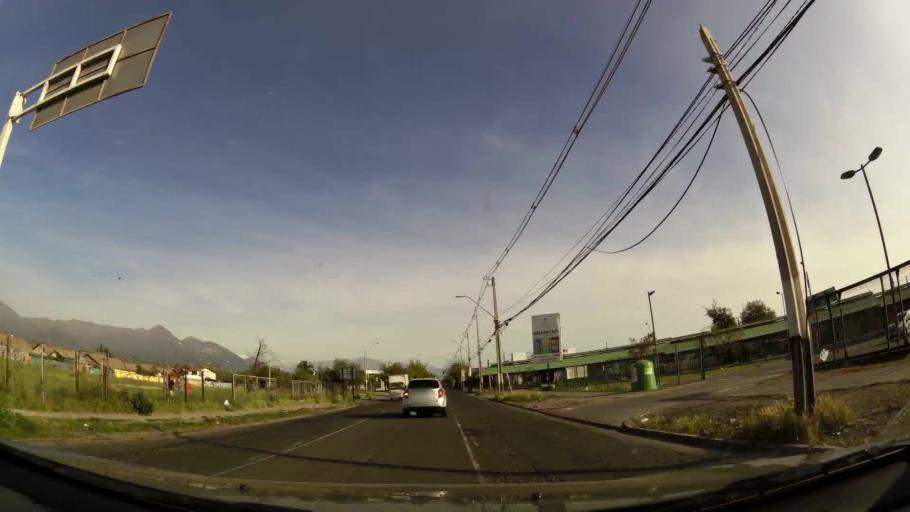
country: CL
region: Santiago Metropolitan
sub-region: Provincia de Cordillera
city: Puente Alto
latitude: -33.5810
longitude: -70.5689
